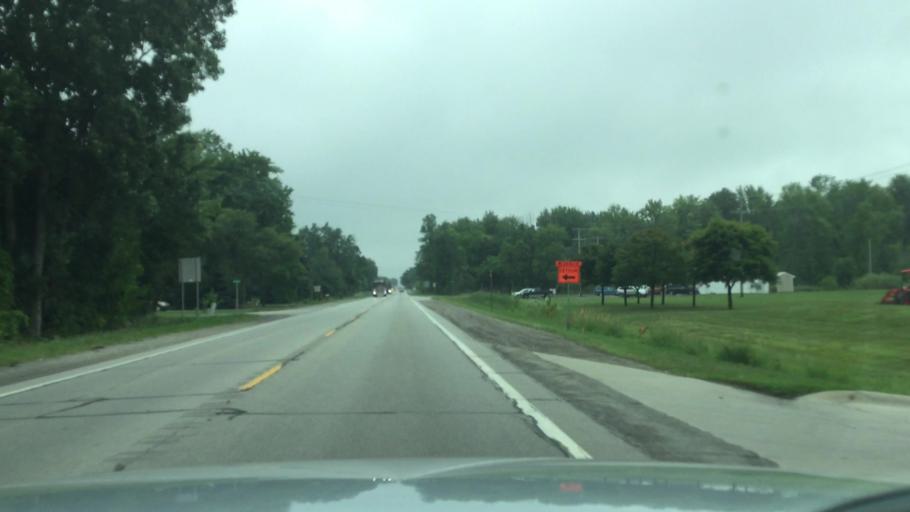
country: US
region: Michigan
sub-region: Shiawassee County
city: Durand
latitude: 42.9695
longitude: -83.9288
